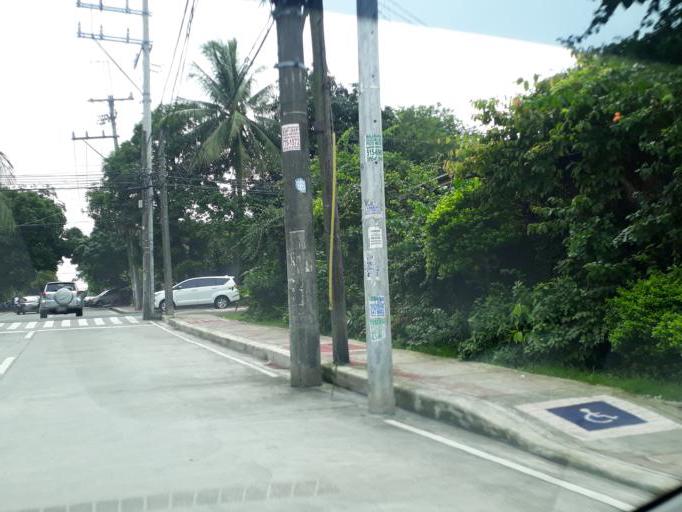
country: PH
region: Calabarzon
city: Del Monte
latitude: 14.6329
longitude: 121.0368
